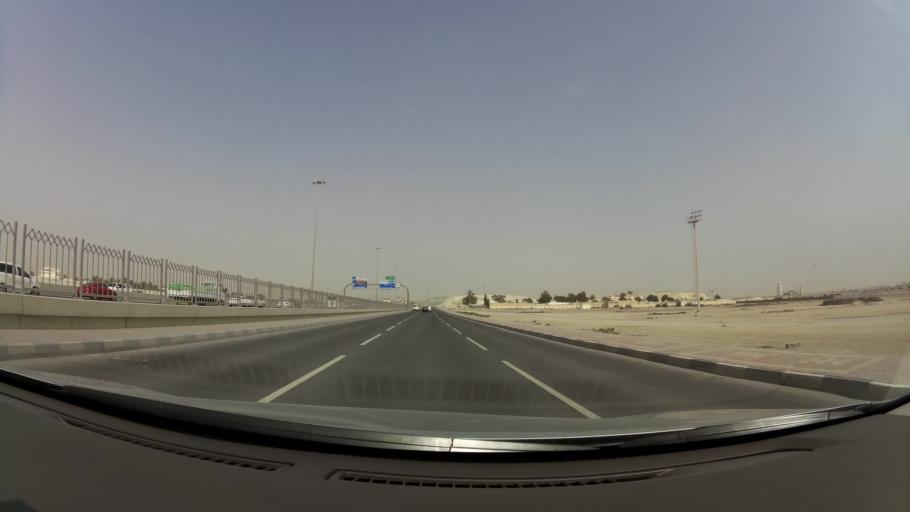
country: QA
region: Baladiyat ad Dawhah
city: Doha
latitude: 25.2827
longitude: 51.4846
